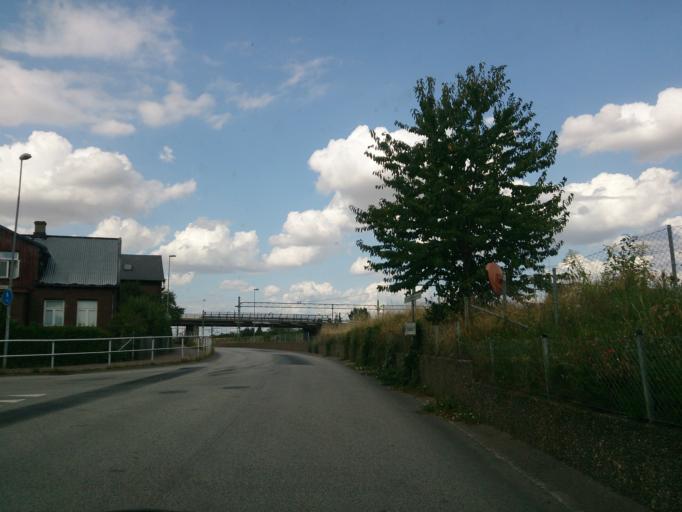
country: SE
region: Skane
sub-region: Kavlinge Kommun
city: Kaevlinge
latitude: 55.7963
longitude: 13.1102
